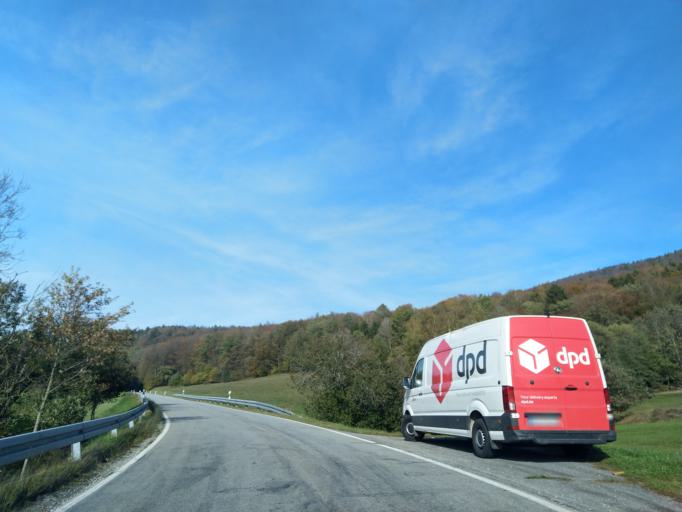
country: DE
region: Bavaria
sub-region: Lower Bavaria
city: Grattersdorf
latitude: 48.7984
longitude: 13.1708
